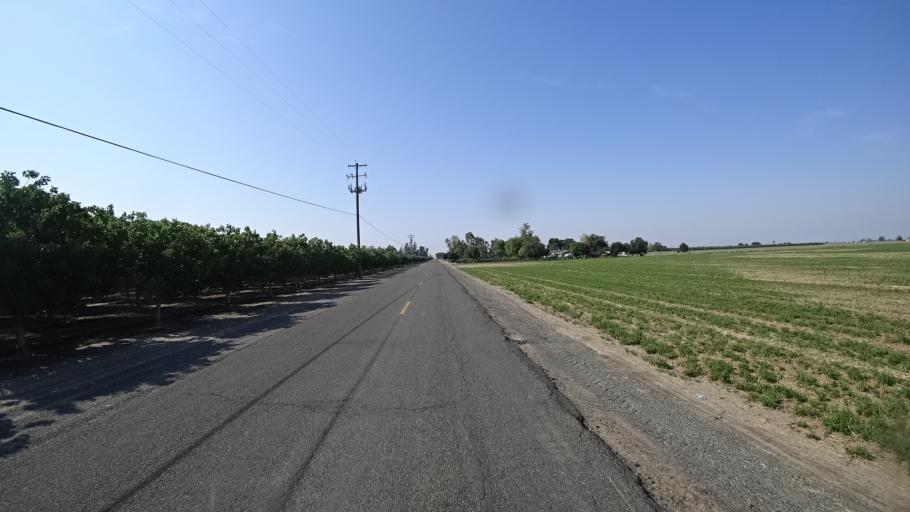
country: US
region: California
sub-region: Kings County
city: Lemoore
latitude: 36.3417
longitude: -119.8513
